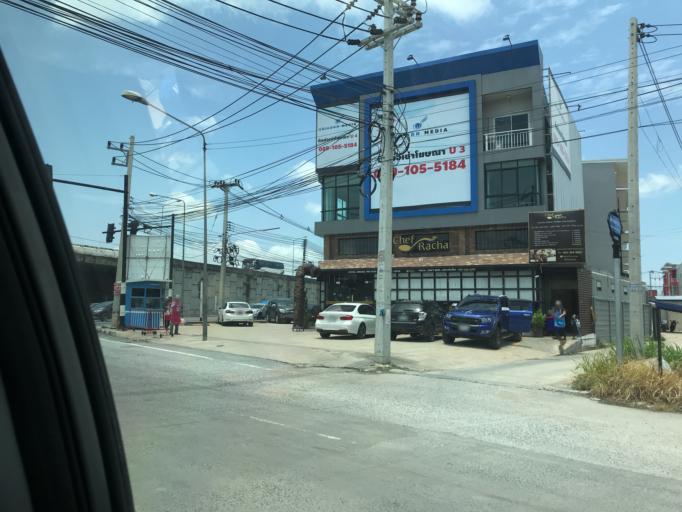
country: TH
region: Chon Buri
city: Si Racha
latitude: 13.1453
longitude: 100.9852
